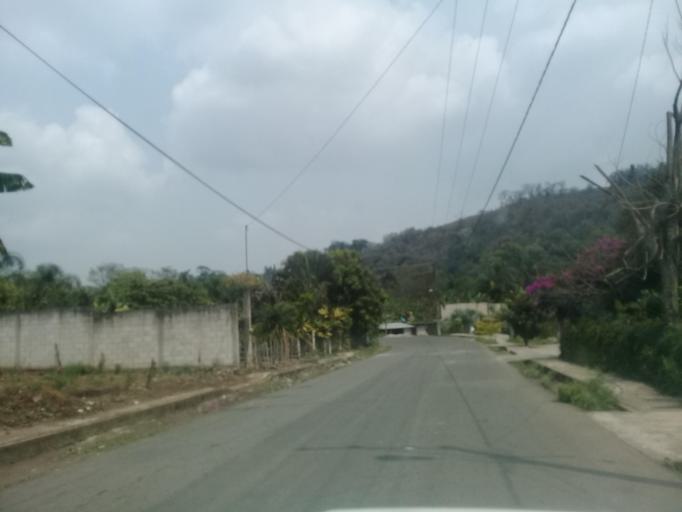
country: MX
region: Veracruz
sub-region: Cordoba
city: San Jose de Tapia
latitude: 18.8250
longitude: -96.9791
